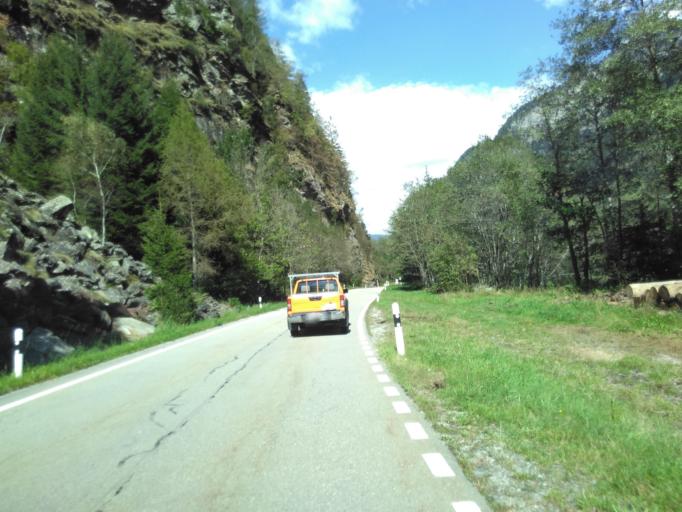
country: CH
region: Grisons
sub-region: Moesa District
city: Arvigo
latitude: 46.3172
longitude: 9.1167
